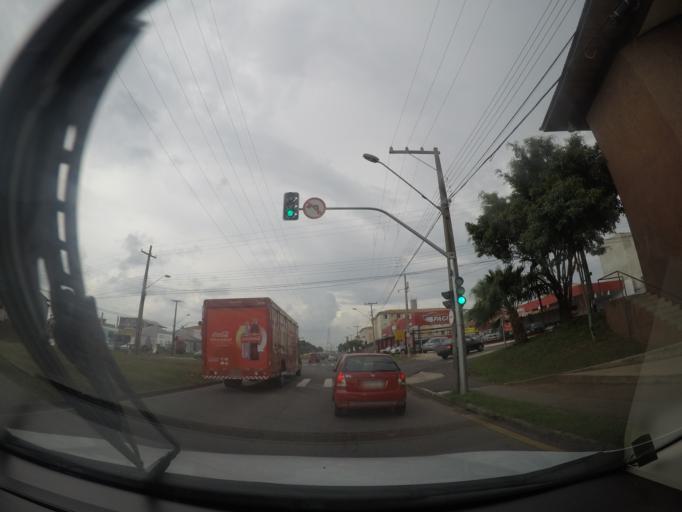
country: BR
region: Parana
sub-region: Sao Jose Dos Pinhais
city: Sao Jose dos Pinhais
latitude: -25.5452
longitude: -49.2652
